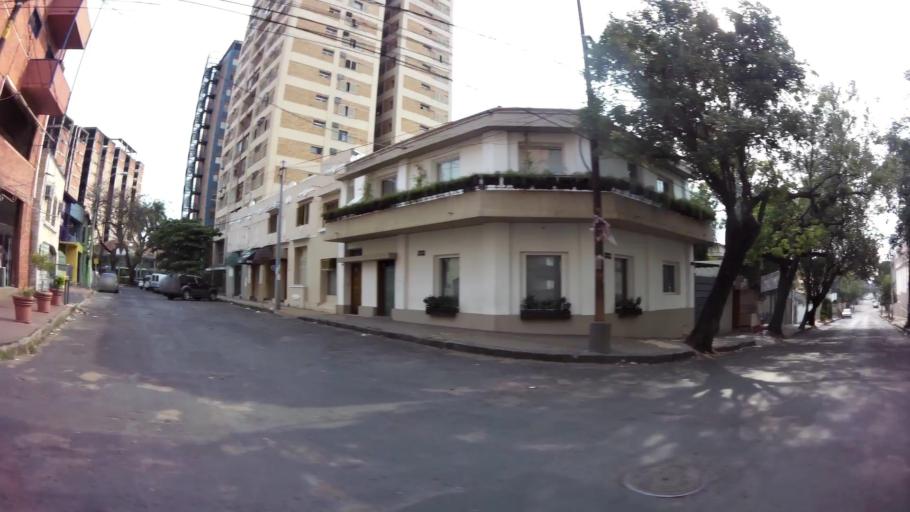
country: PY
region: Asuncion
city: Asuncion
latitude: -25.2873
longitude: -57.6188
